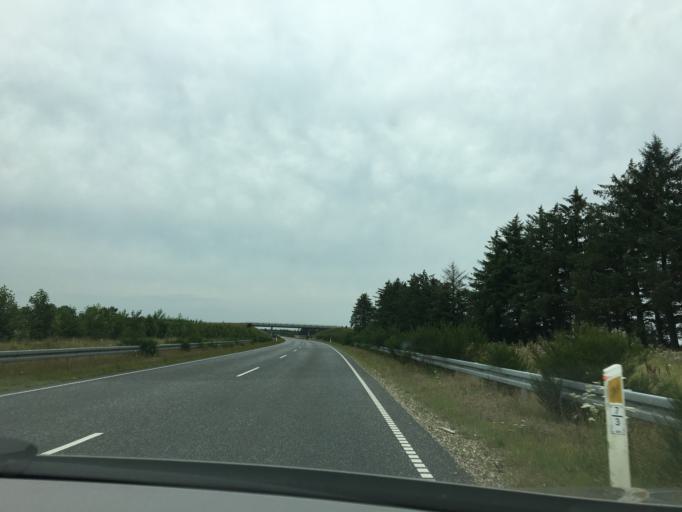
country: DK
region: Central Jutland
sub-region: Herning Kommune
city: Sunds
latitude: 56.1952
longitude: 8.9983
